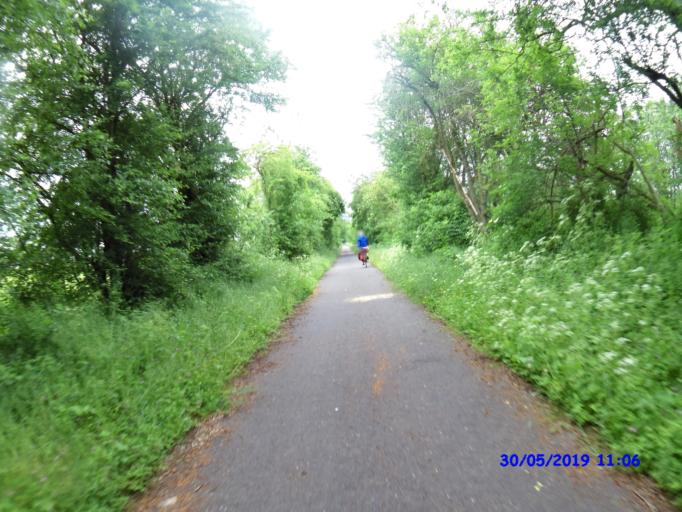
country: BE
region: Wallonia
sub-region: Province du Hainaut
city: Thuin
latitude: 50.2859
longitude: 4.3251
